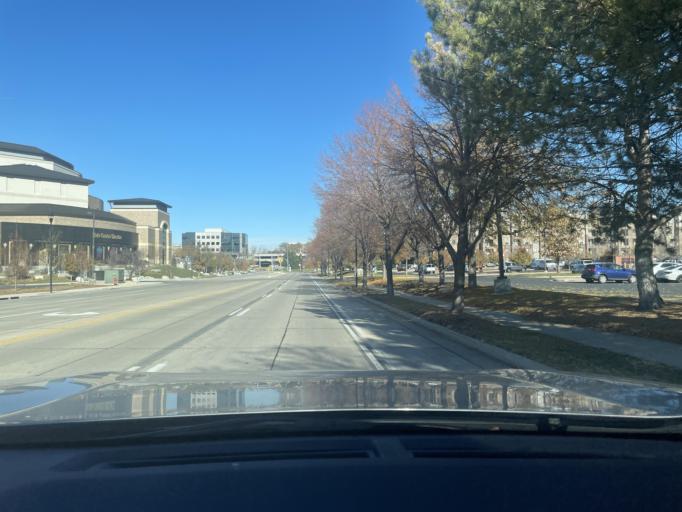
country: US
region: Utah
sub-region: Salt Lake County
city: Sandy City
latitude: 40.5701
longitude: -111.8973
